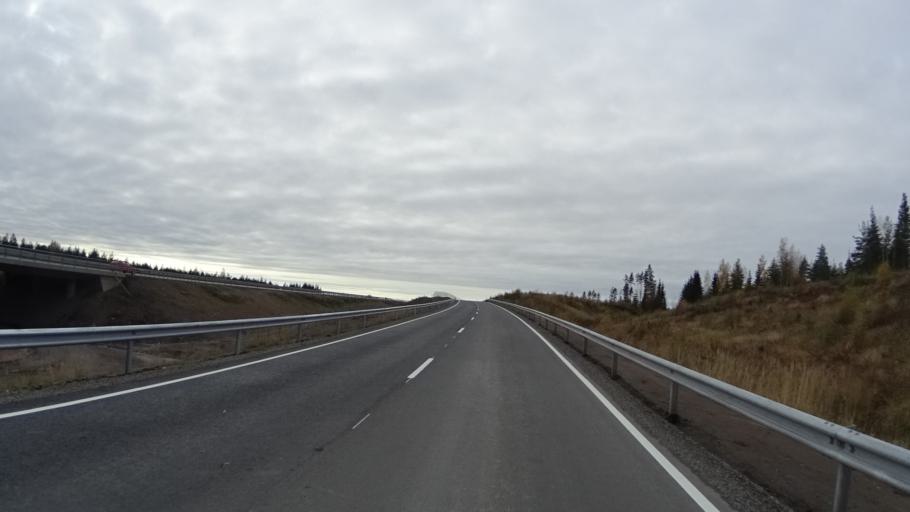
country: FI
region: South Karelia
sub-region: Lappeenranta
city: Lemi
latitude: 61.0010
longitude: 27.9410
